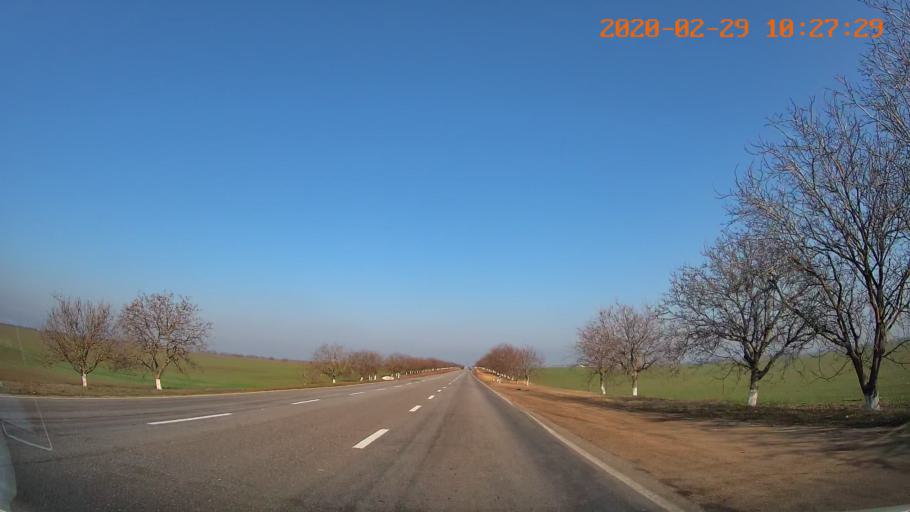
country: MD
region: Telenesti
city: Tiraspolul Nou
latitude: 46.8965
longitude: 29.5975
